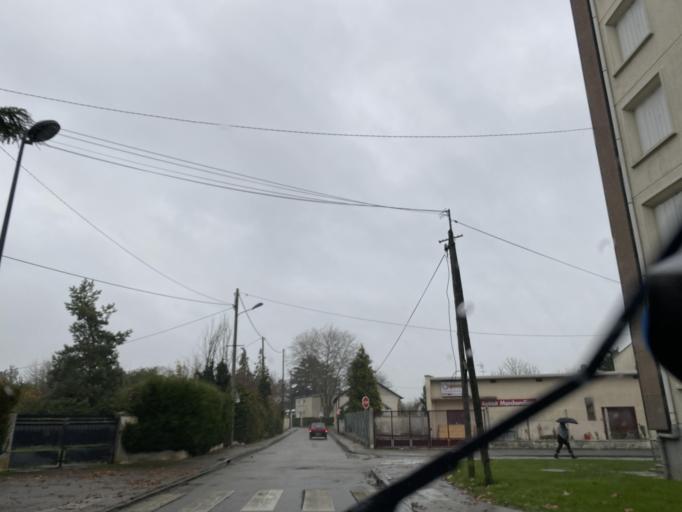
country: FR
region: Haute-Normandie
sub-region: Departement de l'Eure
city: Evreux
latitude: 49.0270
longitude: 1.1735
